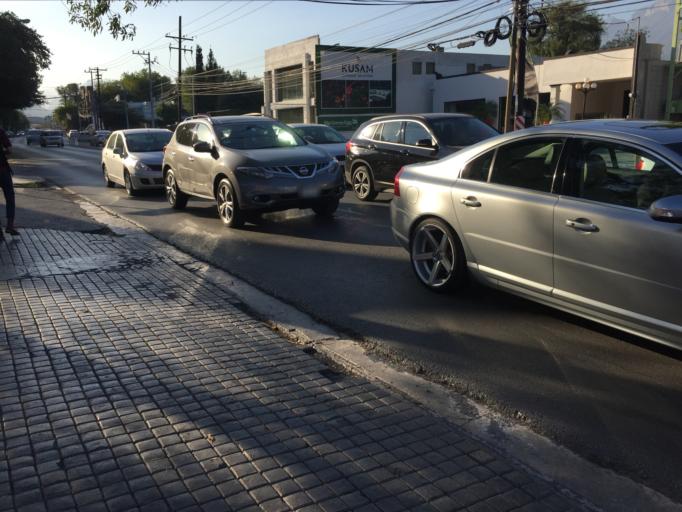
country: MX
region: Nuevo Leon
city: Garza Garcia
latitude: 25.6517
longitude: -100.3664
